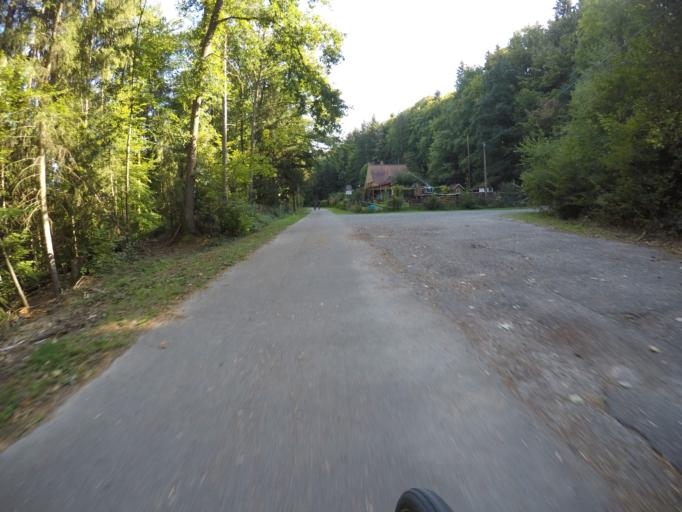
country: DE
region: Baden-Wuerttemberg
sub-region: Regierungsbezirk Stuttgart
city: Steinenbronn
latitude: 48.6752
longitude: 9.1263
